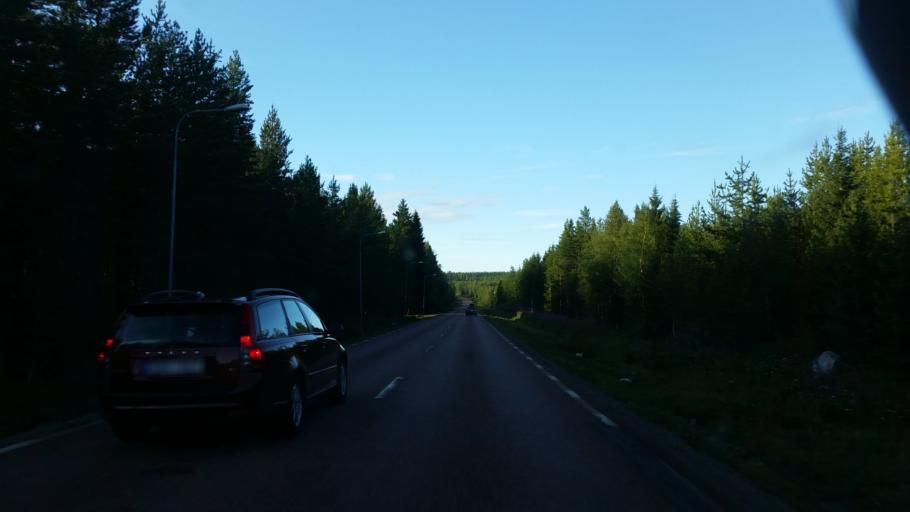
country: SE
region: Vaesterbotten
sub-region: Dorotea Kommun
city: Dorotea
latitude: 64.0728
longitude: 16.0830
